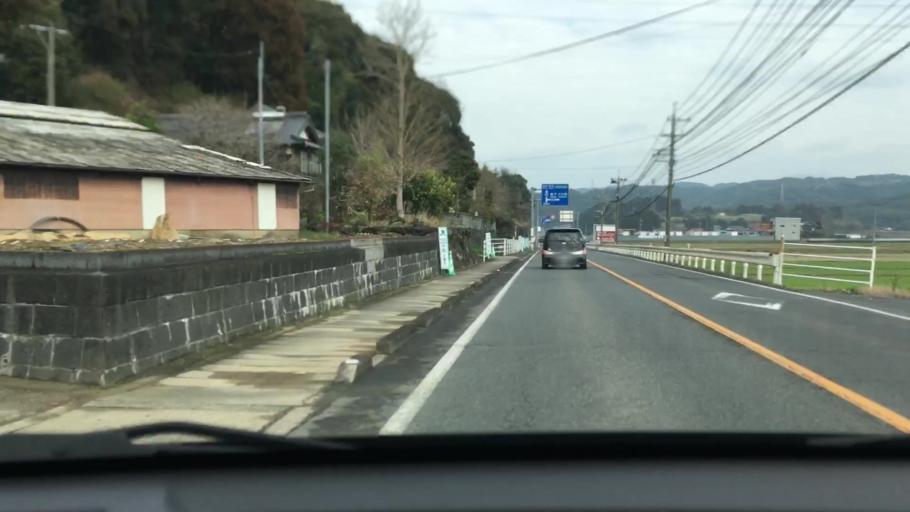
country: JP
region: Saga Prefecture
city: Imaricho-ko
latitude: 33.3045
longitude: 129.9230
